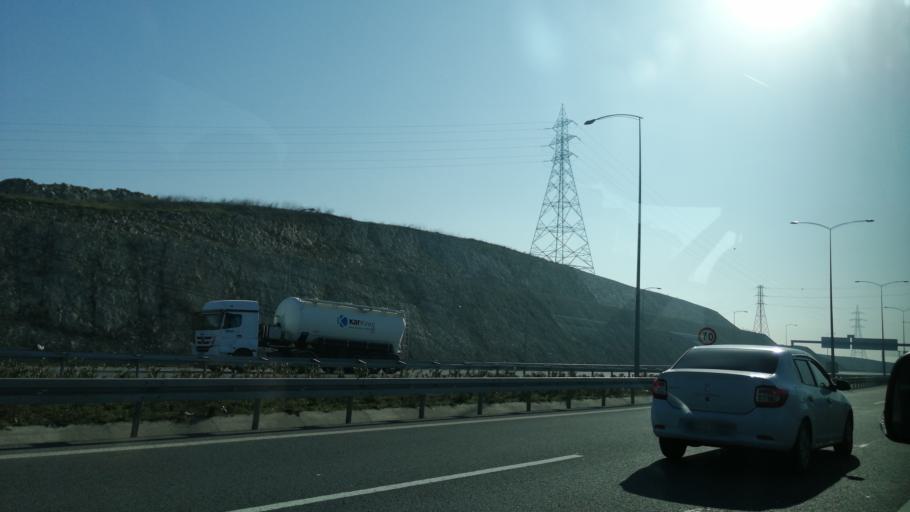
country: TR
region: Kocaeli
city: Tavsanli
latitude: 40.7942
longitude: 29.5107
